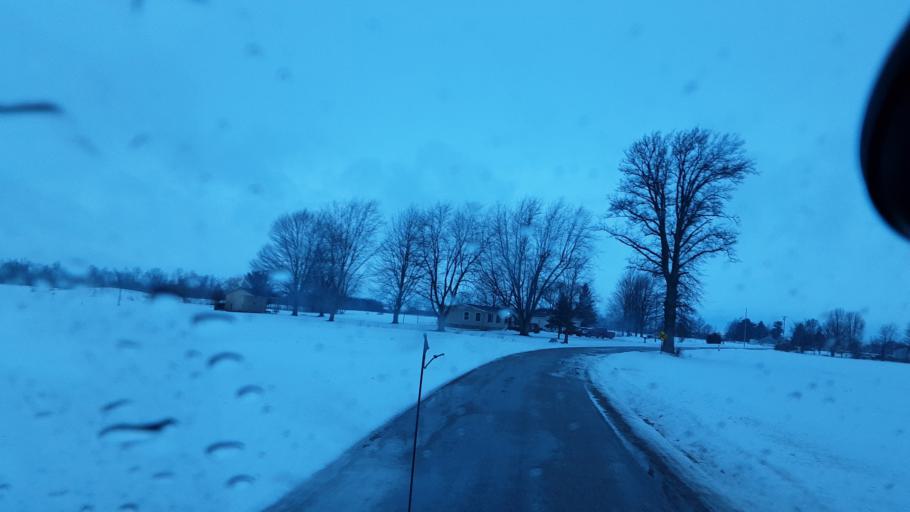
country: US
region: Ohio
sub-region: Morrow County
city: Mount Gilead
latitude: 40.6625
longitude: -82.9167
